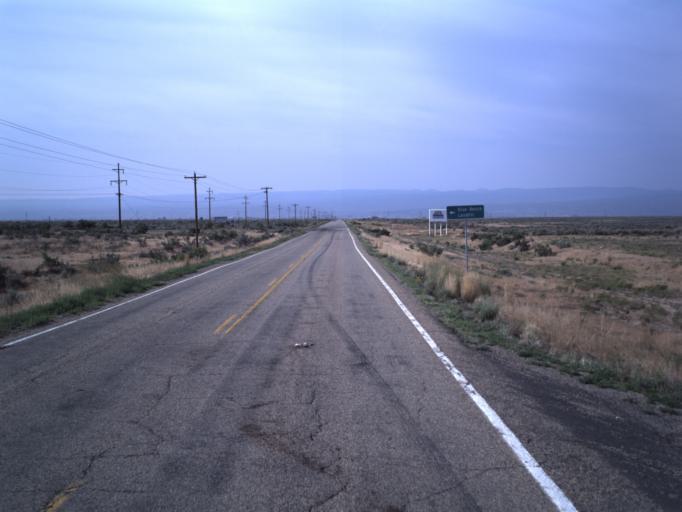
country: US
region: Utah
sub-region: Duchesne County
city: Duchesne
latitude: 40.2731
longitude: -110.3804
